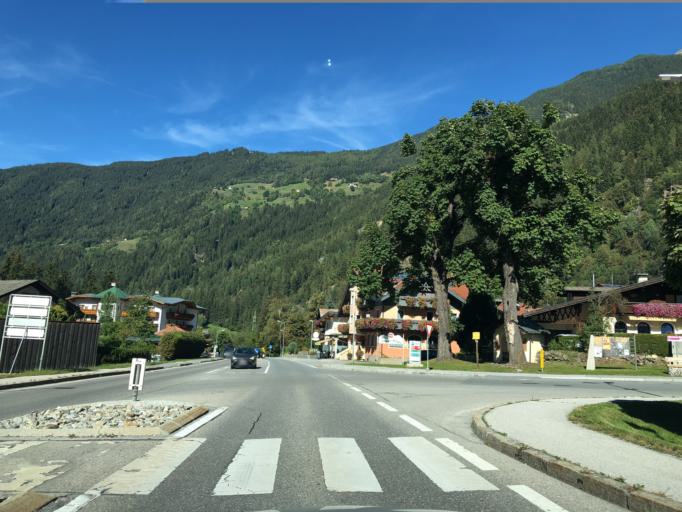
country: AT
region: Tyrol
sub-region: Politischer Bezirk Imst
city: Oetz
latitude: 47.1916
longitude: 10.9070
